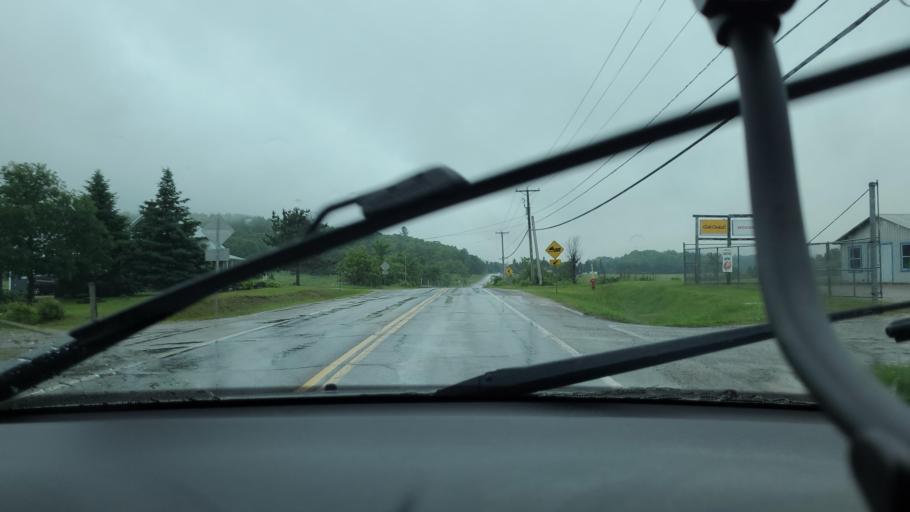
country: CA
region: Quebec
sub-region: Outaouais
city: Saint-Andre-Avellin
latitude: 45.7132
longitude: -75.0559
